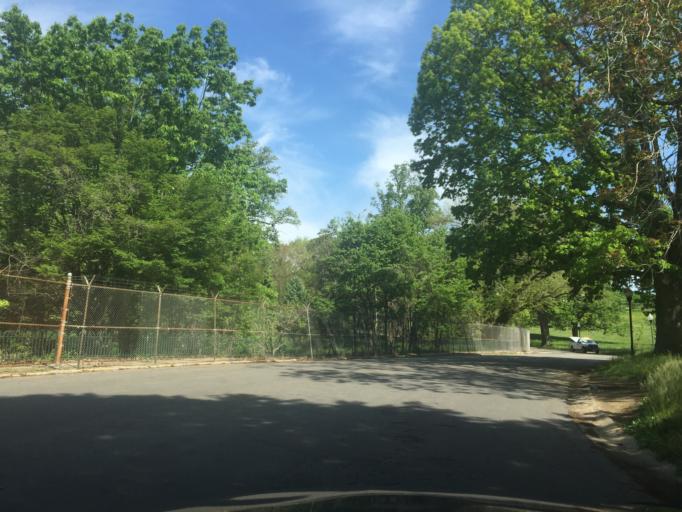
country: US
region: Maryland
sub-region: City of Baltimore
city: Baltimore
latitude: 39.3211
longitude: -76.6460
